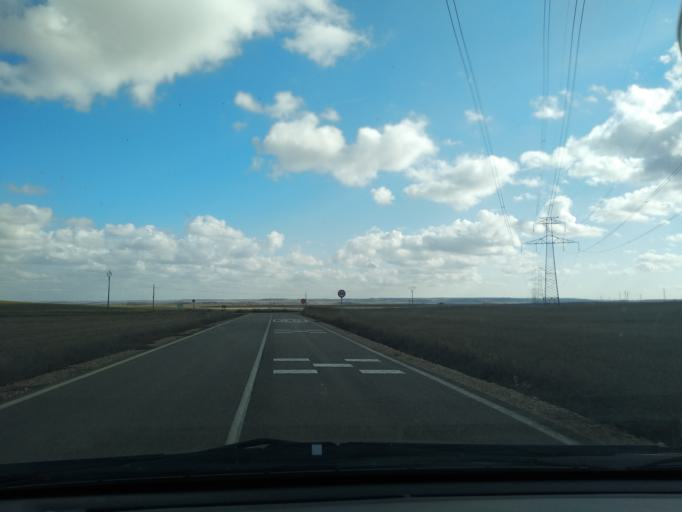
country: ES
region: Castille and Leon
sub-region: Provincia de Valladolid
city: Berrueces
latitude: 41.9476
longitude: -5.0692
